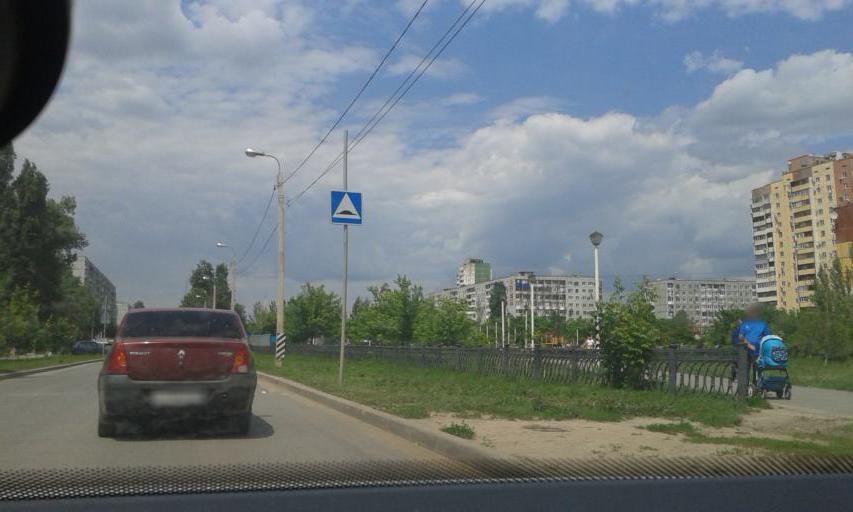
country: RU
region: Volgograd
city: Volgograd
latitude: 48.7518
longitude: 44.5041
